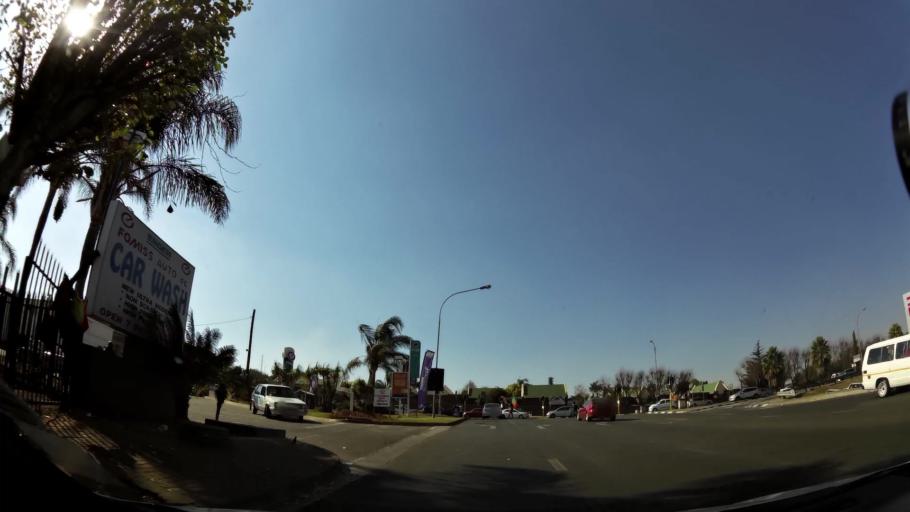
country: ZA
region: Gauteng
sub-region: City of Johannesburg Metropolitan Municipality
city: Johannesburg
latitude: -26.2666
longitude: 28.0599
